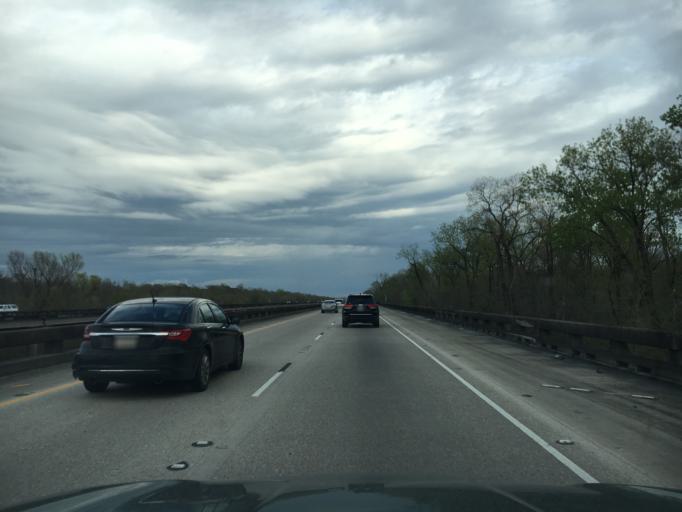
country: US
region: Louisiana
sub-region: Iberville Parish
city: Maringouin
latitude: 30.3723
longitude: -91.6116
